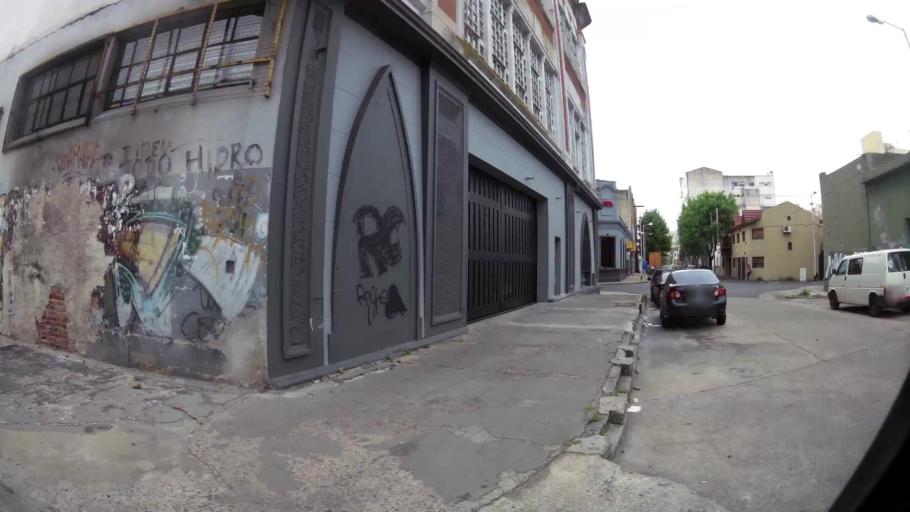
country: AR
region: Buenos Aires
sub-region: Partido de Avellaneda
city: Avellaneda
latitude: -34.6647
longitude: -58.3573
